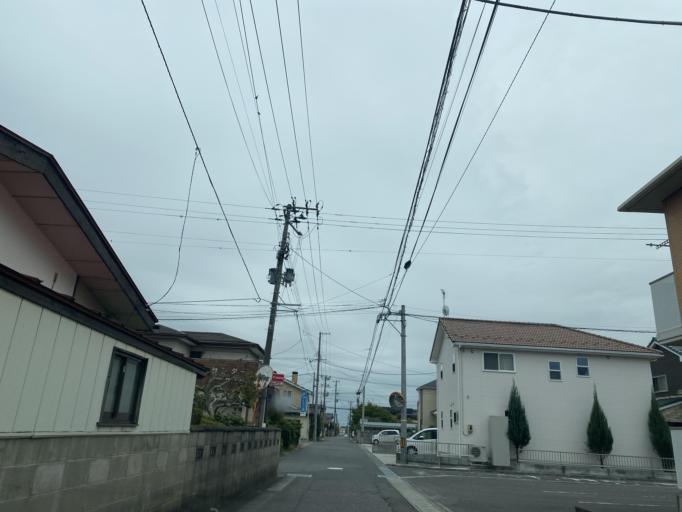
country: JP
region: Fukushima
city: Koriyama
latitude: 37.3806
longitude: 140.3545
